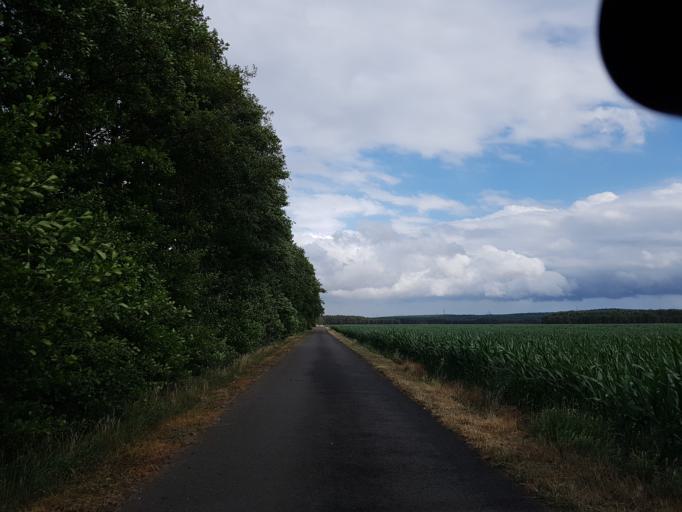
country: DE
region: Saxony-Anhalt
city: Jessen
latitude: 51.8339
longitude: 12.9520
